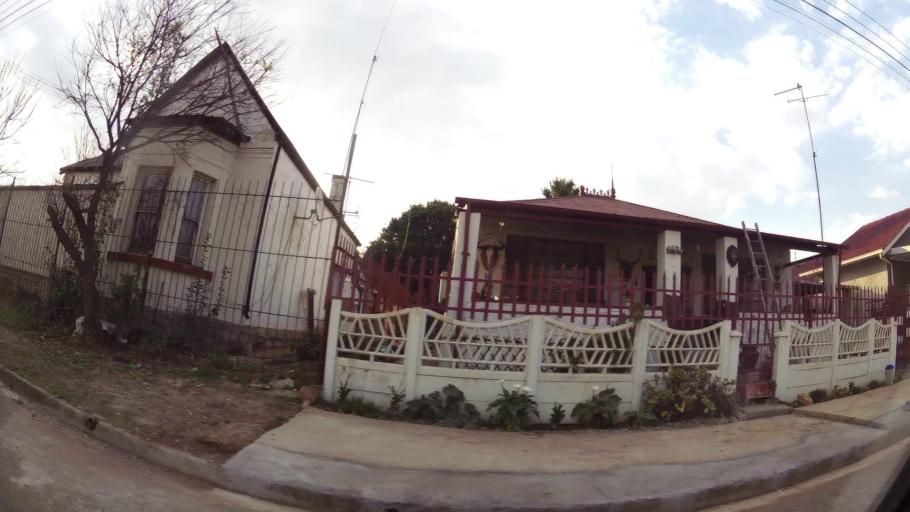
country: ZA
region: Gauteng
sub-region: Ekurhuleni Metropolitan Municipality
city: Germiston
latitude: -26.2458
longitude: 28.2019
